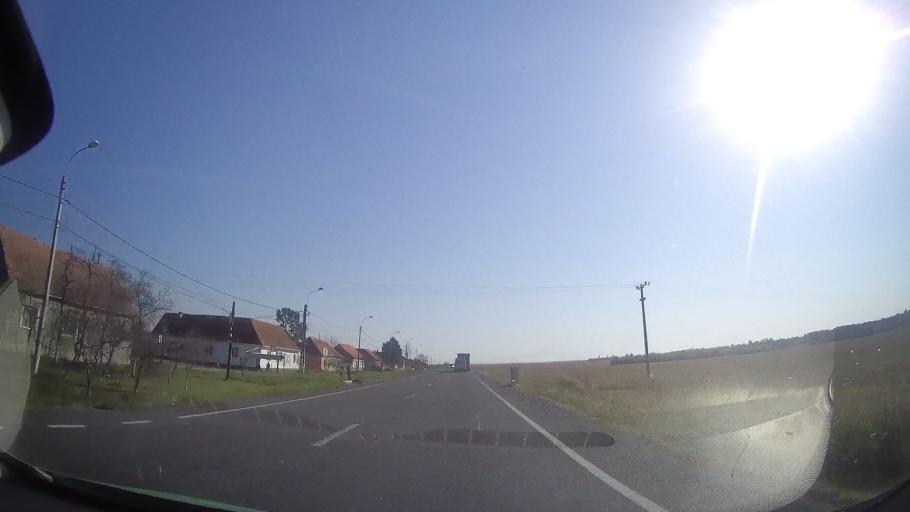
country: RO
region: Timis
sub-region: Comuna Topolovatu Mare
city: Topolovatu Mare
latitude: 45.7781
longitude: 21.6785
